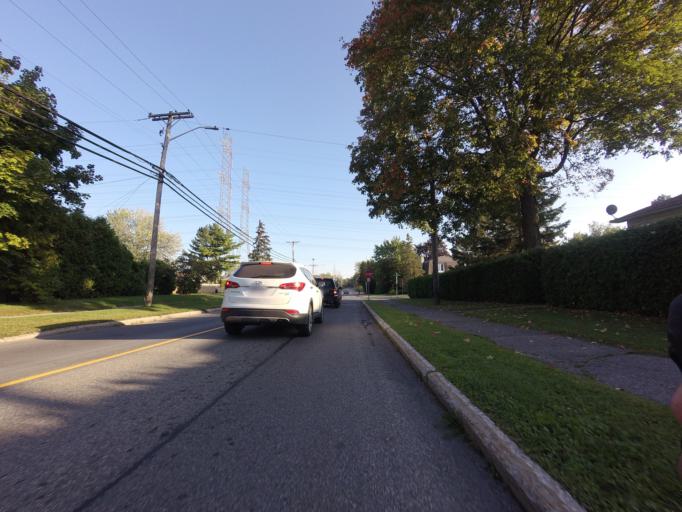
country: CA
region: Ontario
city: Ottawa
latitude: 45.3608
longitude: -75.6750
